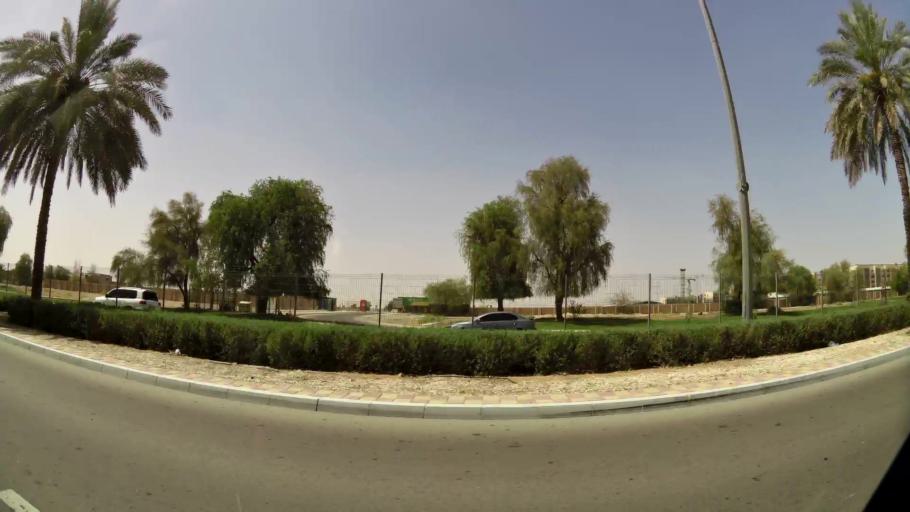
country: AE
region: Abu Dhabi
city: Al Ain
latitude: 24.2426
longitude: 55.7110
